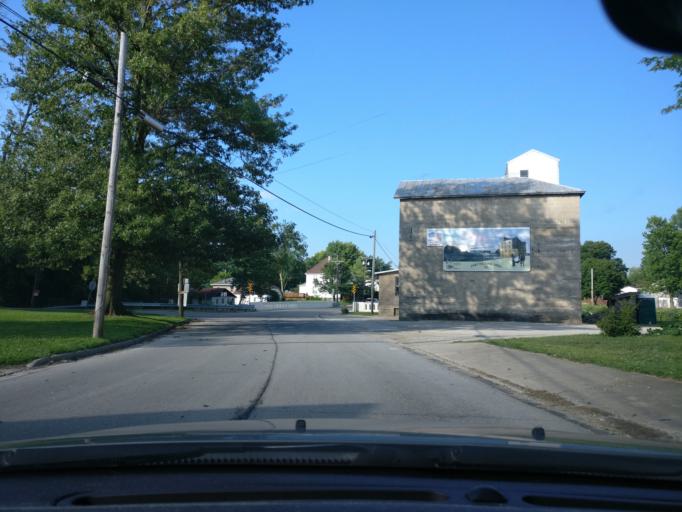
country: US
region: Ohio
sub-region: Greene County
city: Shawnee Hills
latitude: 39.5508
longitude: -83.7883
